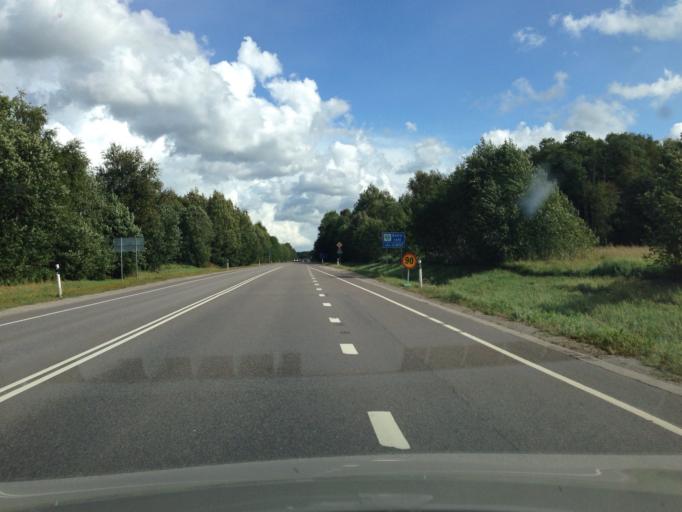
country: EE
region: Harju
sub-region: Saue linn
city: Saue
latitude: 59.3125
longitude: 24.5847
